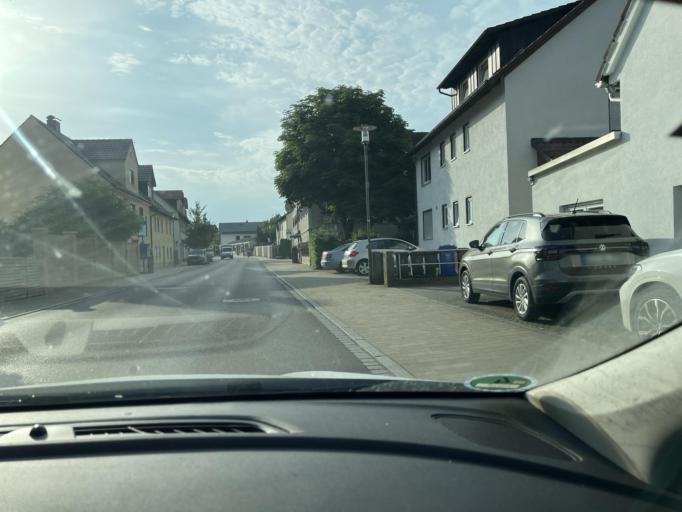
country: DE
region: Bavaria
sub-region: Swabia
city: Aindling
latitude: 48.5132
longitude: 10.9575
